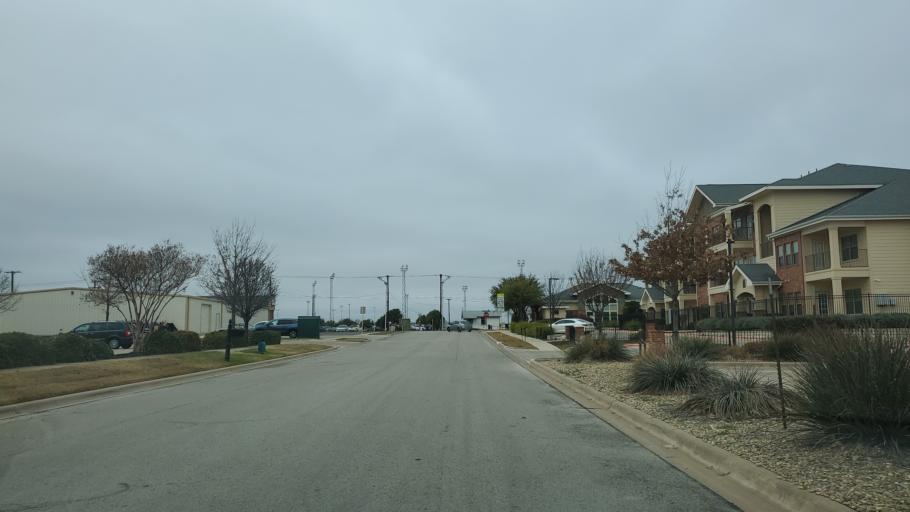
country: US
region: Texas
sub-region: Bell County
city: Killeen
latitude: 31.0845
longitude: -97.7349
